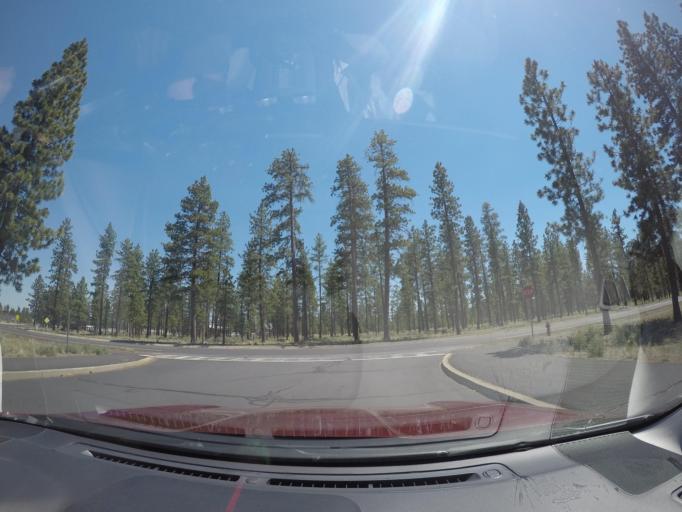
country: US
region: Oregon
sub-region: Deschutes County
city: Sisters
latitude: 44.2949
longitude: -121.5756
